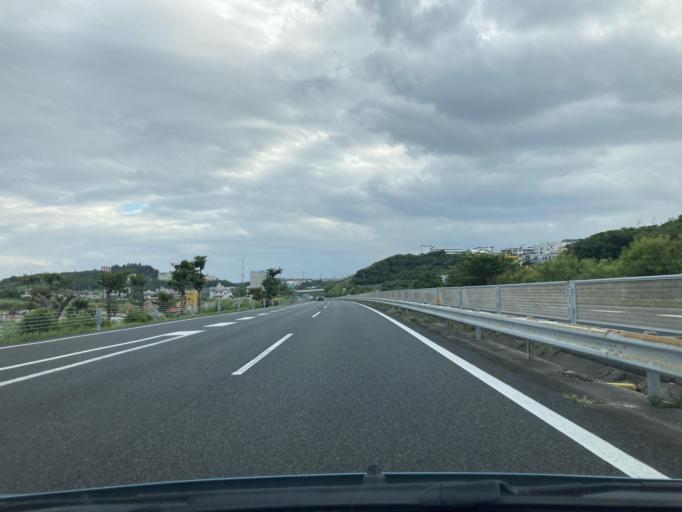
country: JP
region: Okinawa
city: Ginowan
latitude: 26.2387
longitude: 127.7416
